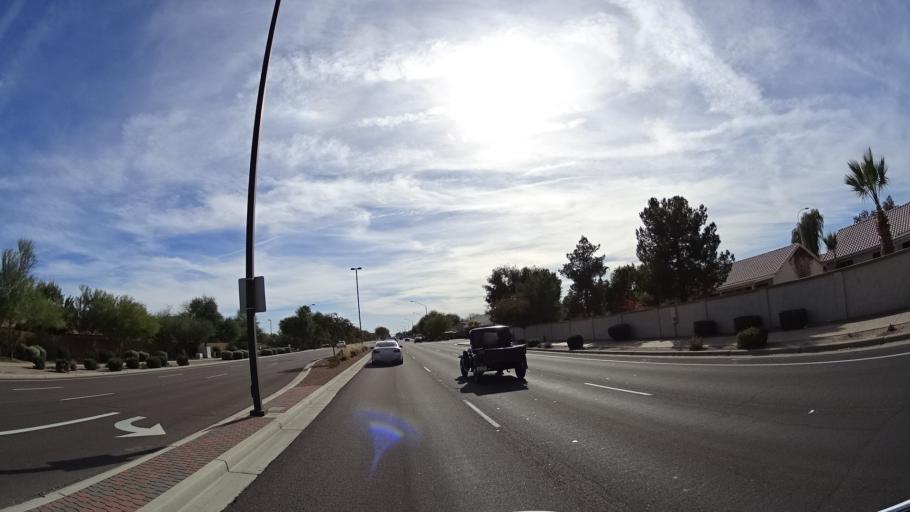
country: US
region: Arizona
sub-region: Maricopa County
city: Chandler
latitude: 33.2999
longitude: -111.7899
